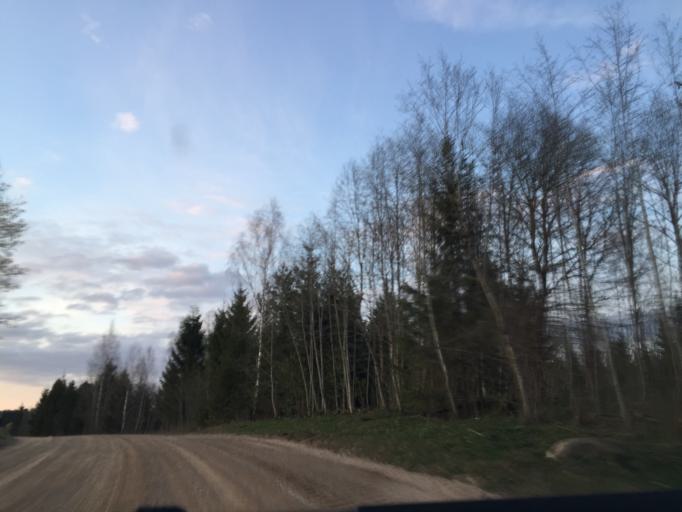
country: LV
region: Aluksnes Rajons
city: Aluksne
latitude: 57.3368
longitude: 26.9604
